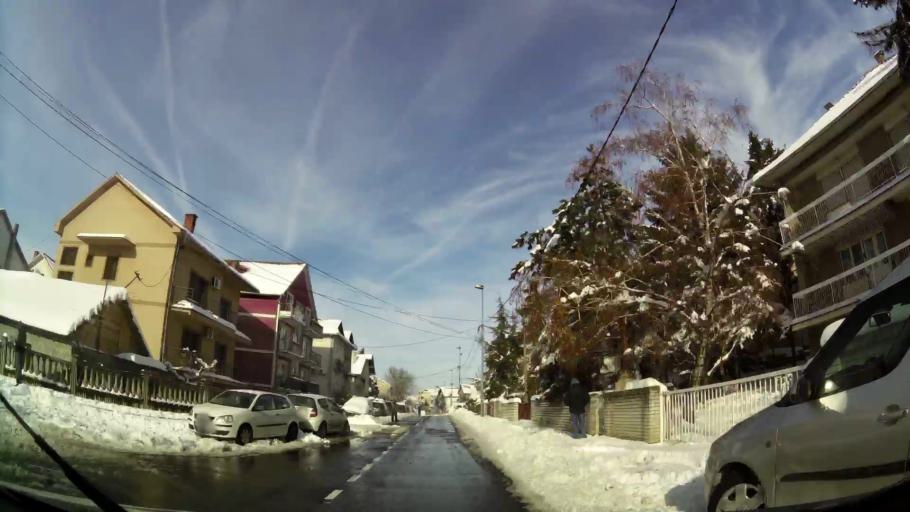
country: RS
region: Central Serbia
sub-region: Belgrade
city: Zvezdara
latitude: 44.7928
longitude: 20.5347
